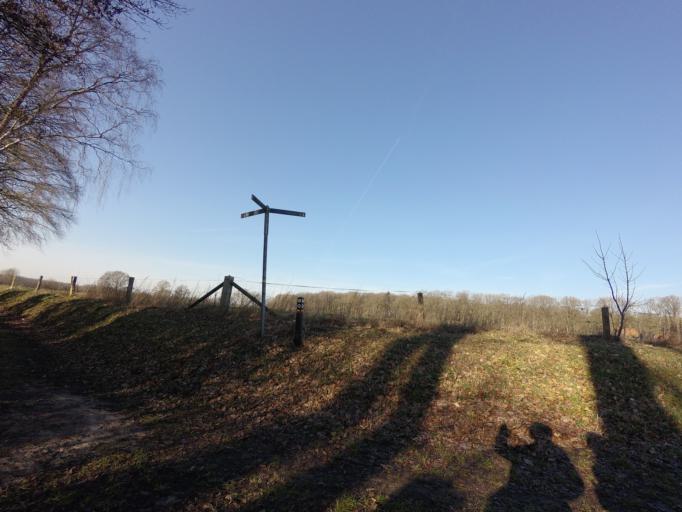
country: NL
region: Gelderland
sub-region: Gemeente Lochem
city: Barchem
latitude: 52.1365
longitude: 6.4351
